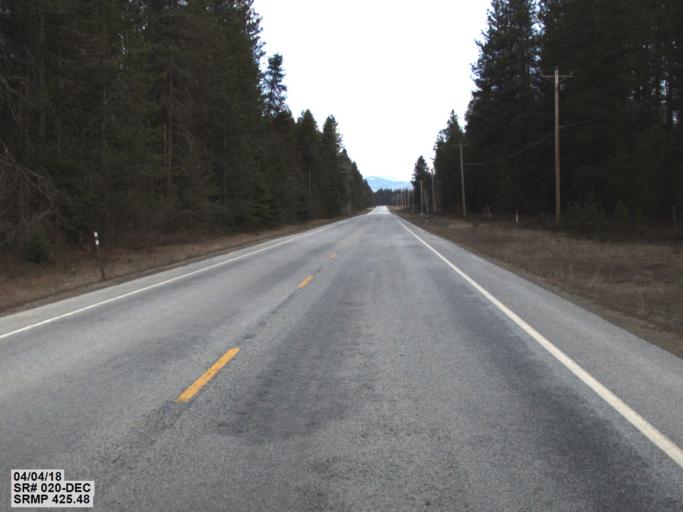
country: US
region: Washington
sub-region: Pend Oreille County
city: Newport
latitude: 48.2537
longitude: -117.2451
